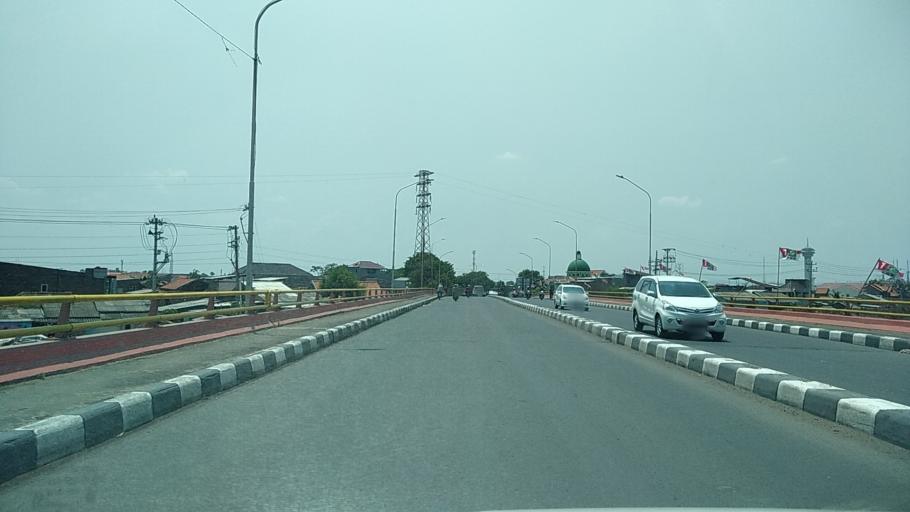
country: ID
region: Central Java
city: Semarang
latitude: -6.9729
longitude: 110.4429
